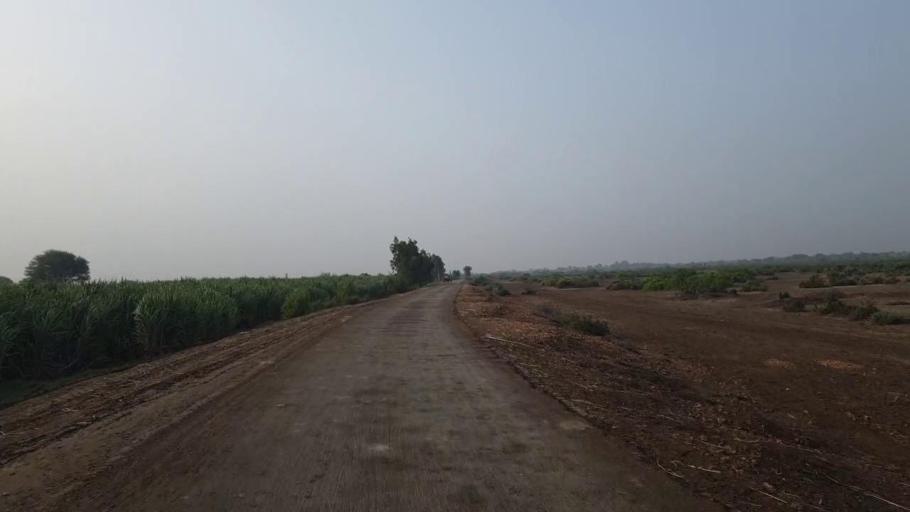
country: PK
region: Sindh
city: Tando Muhammad Khan
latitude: 25.1551
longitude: 68.6095
